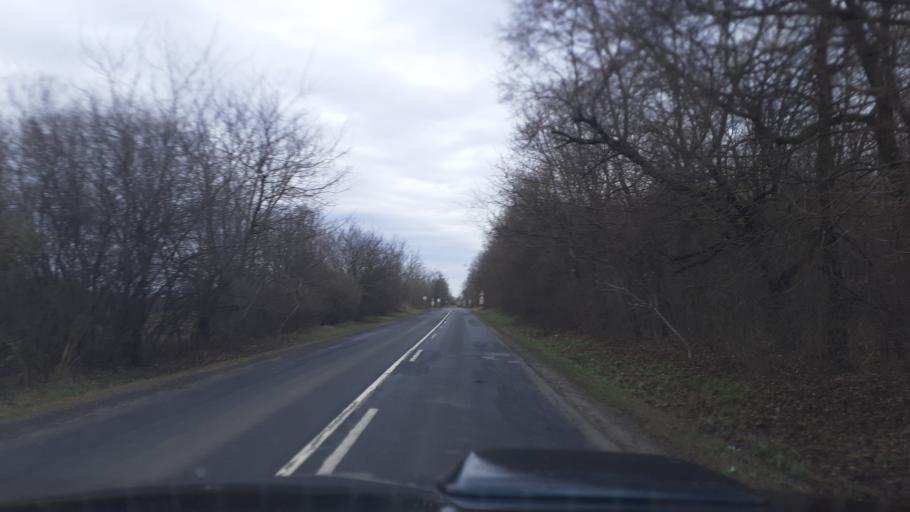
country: HU
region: Fejer
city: Mezofalva
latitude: 46.9733
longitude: 18.7219
